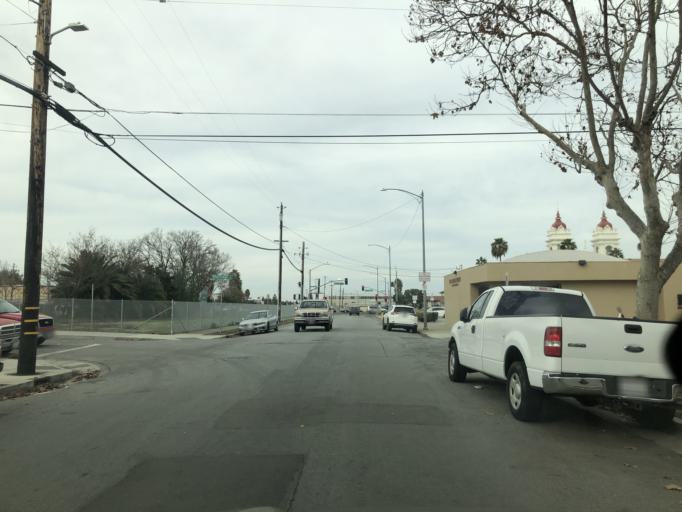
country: US
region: California
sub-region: Santa Clara County
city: San Jose
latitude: 37.3477
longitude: -121.8633
